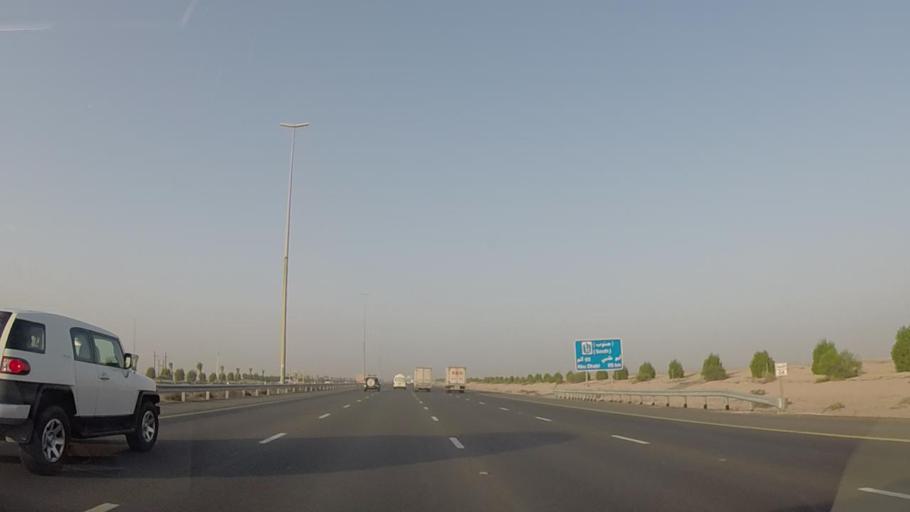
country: AE
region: Dubai
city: Dubai
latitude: 24.9122
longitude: 54.9629
